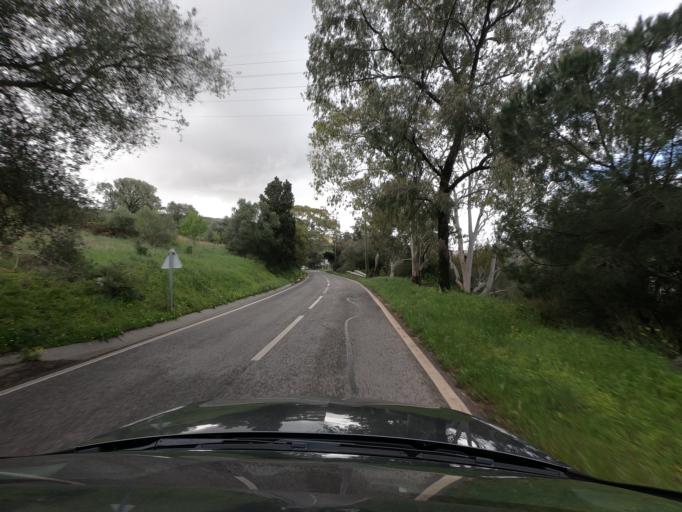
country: PT
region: Lisbon
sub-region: Oeiras
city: Quejas
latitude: 38.7379
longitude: -9.2608
